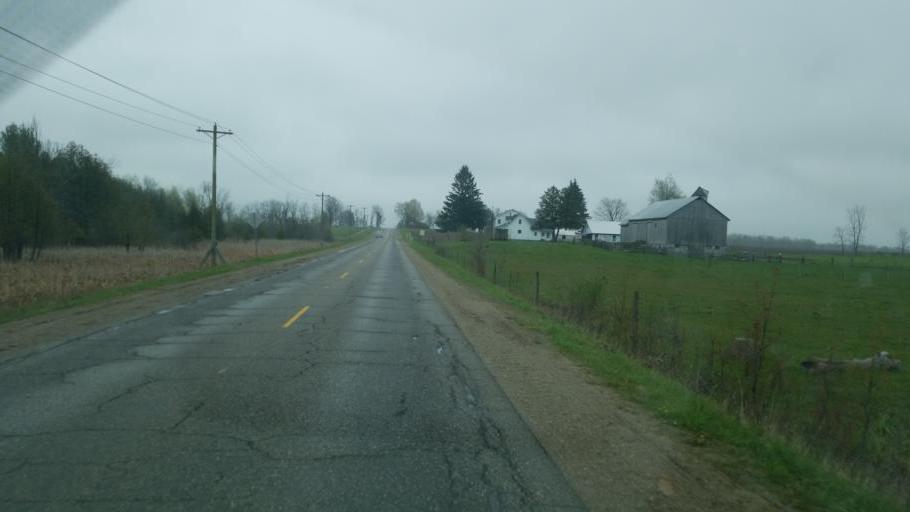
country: US
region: Michigan
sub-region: Mecosta County
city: Canadian Lakes
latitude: 43.5424
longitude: -85.3756
